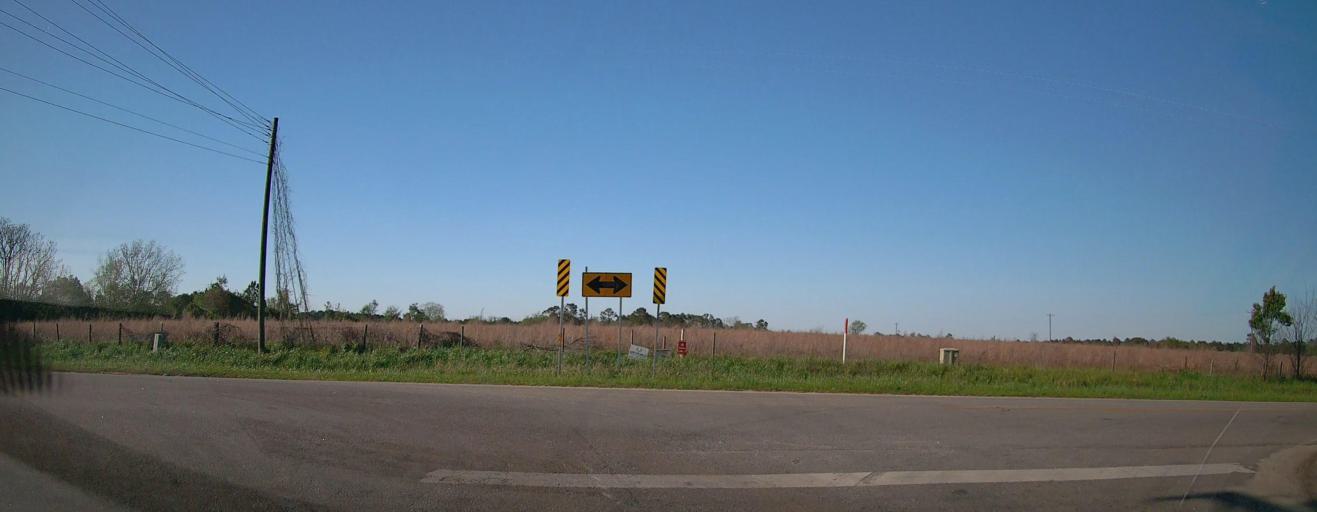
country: US
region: Georgia
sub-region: Ben Hill County
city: Fitzgerald
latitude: 31.7430
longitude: -83.2347
